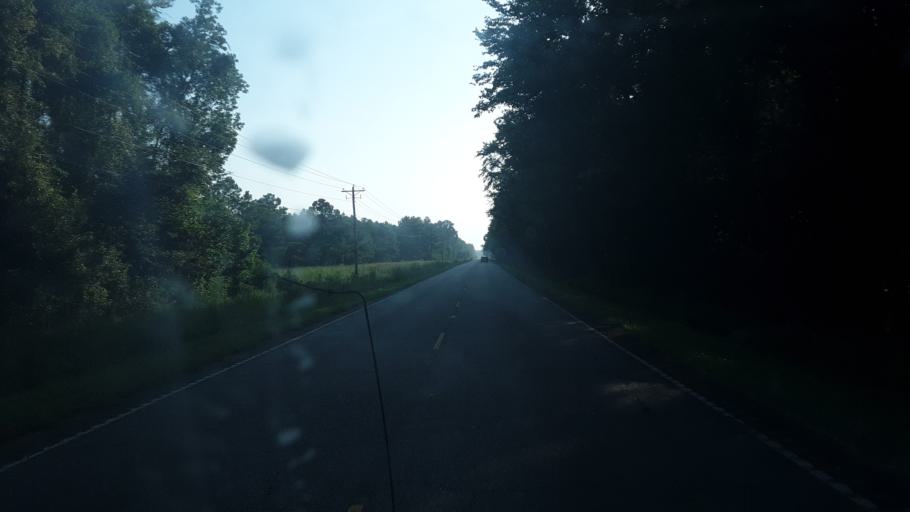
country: US
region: South Carolina
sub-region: Horry County
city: Myrtle Beach
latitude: 33.8432
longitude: -78.8578
